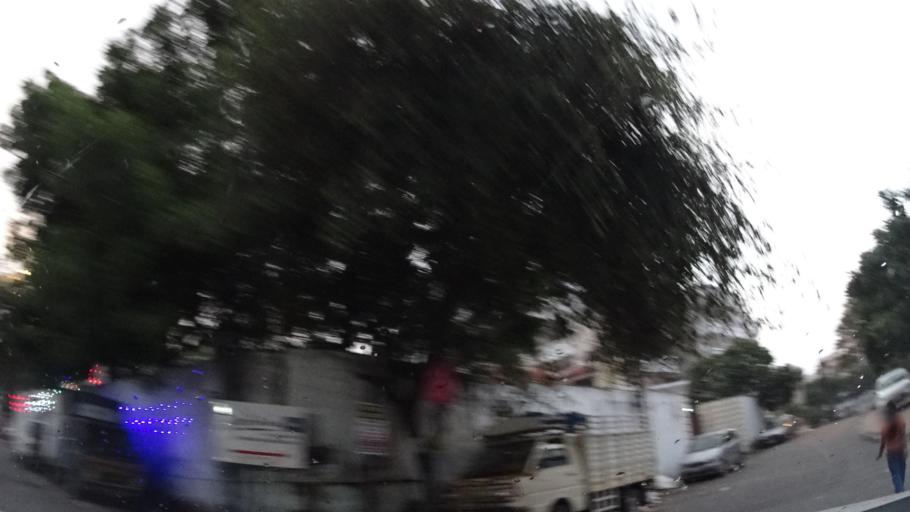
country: IN
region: Telangana
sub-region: Hyderabad
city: Hyderabad
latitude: 17.4208
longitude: 78.4433
